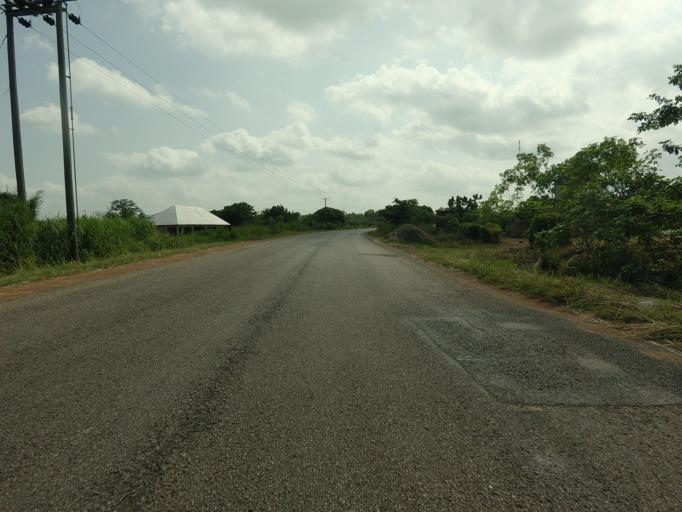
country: GH
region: Volta
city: Ho
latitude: 6.4154
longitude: 0.7490
